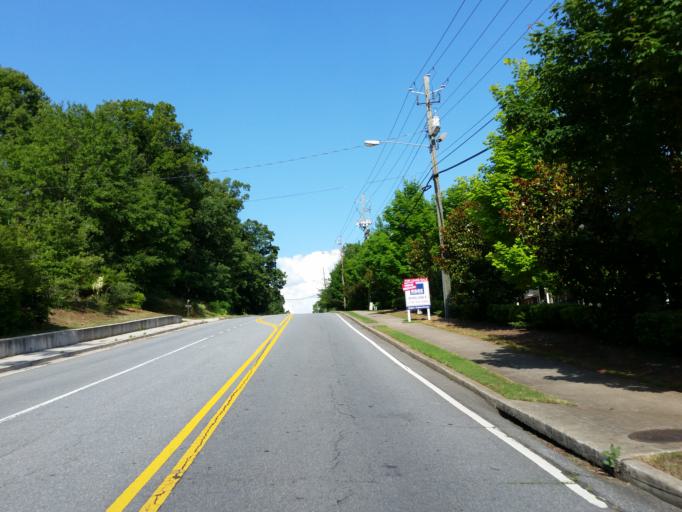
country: US
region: Georgia
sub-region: Fulton County
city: Alpharetta
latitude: 34.0610
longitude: -84.3292
